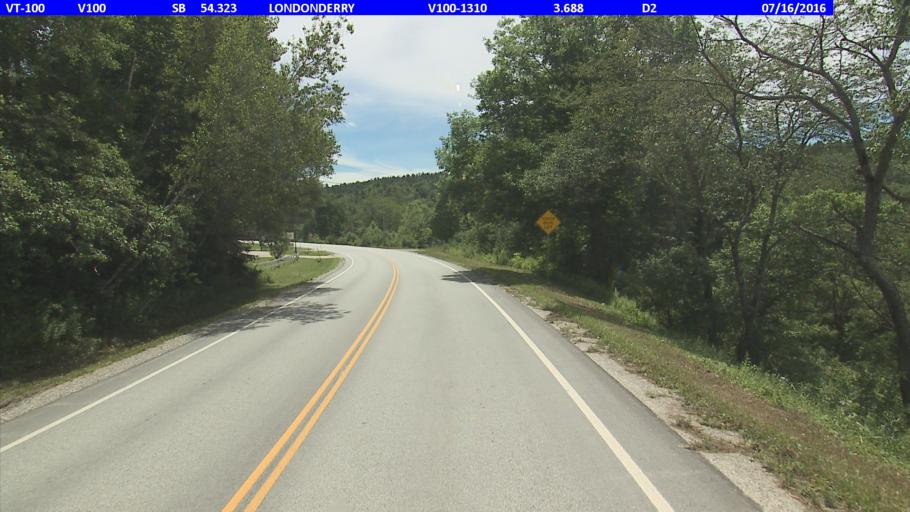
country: US
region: Vermont
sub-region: Windsor County
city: Chester
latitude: 43.2009
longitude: -72.8216
